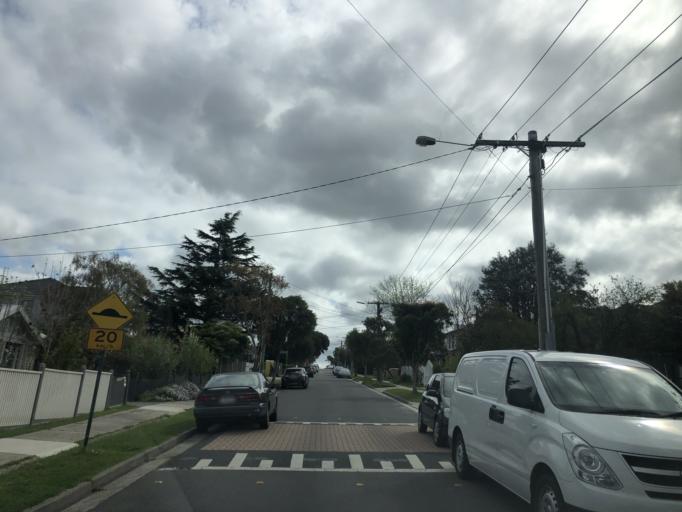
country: AU
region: Victoria
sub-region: Monash
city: Chadstone
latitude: -37.8841
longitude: 145.0987
